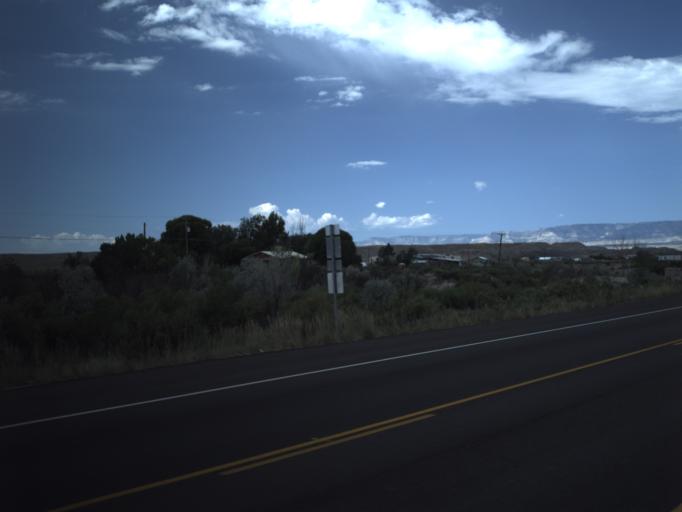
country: US
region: Utah
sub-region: Carbon County
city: Wellington
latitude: 39.5426
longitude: -110.6872
